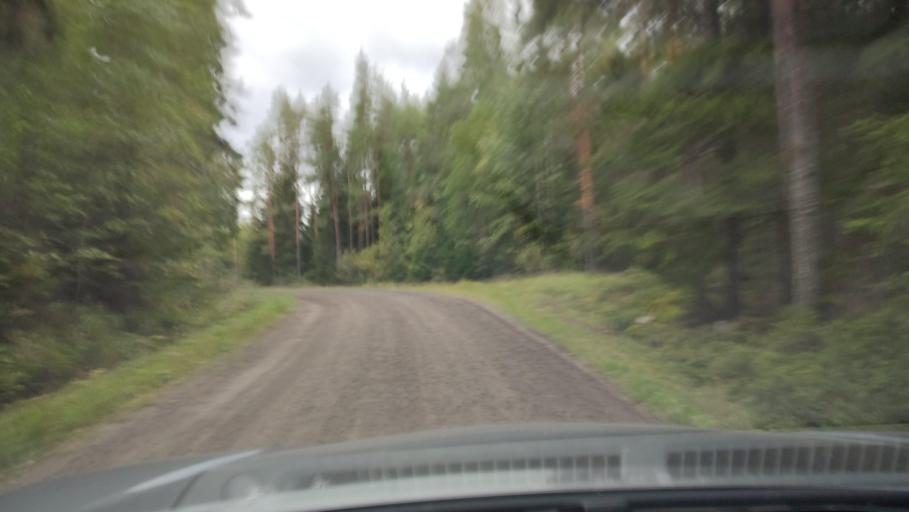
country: FI
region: Southern Ostrobothnia
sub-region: Suupohja
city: Karijoki
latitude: 62.2314
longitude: 21.5735
